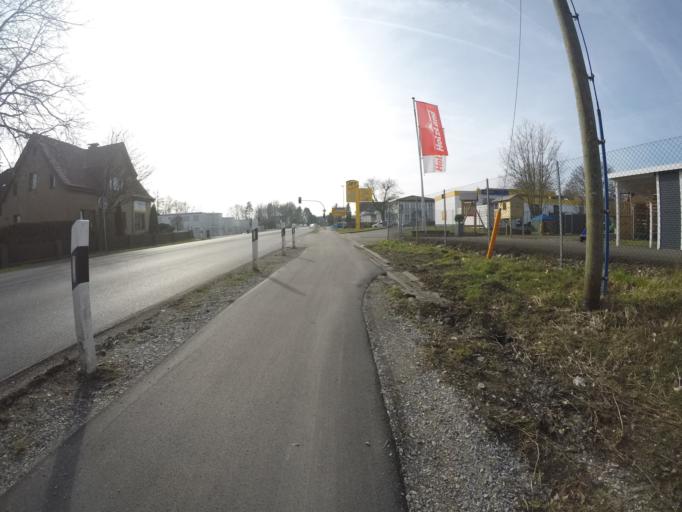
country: DE
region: North Rhine-Westphalia
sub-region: Regierungsbezirk Detmold
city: Herford
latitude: 52.0687
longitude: 8.6128
